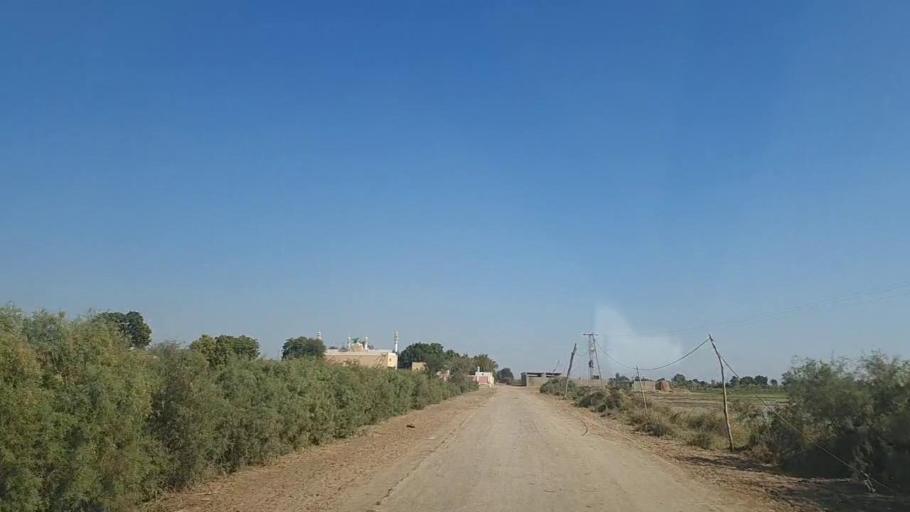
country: PK
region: Sindh
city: Sanghar
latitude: 26.2204
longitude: 68.9618
